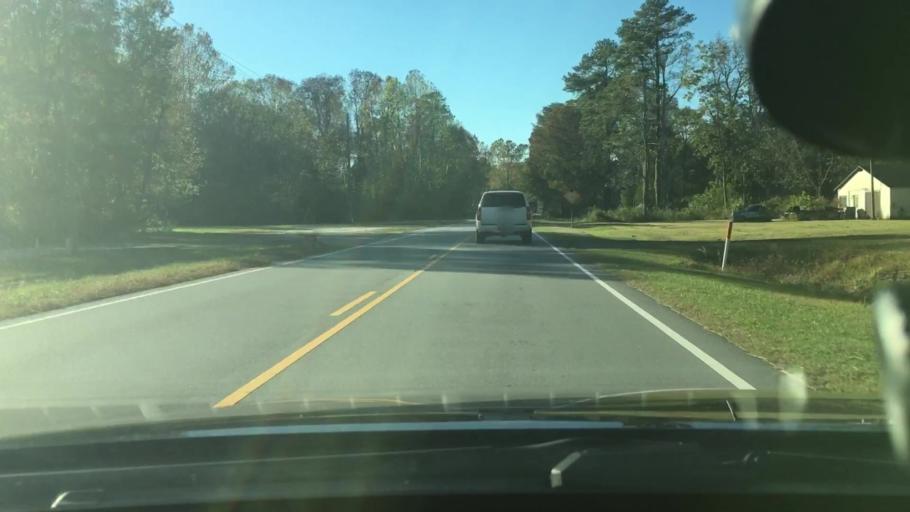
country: US
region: North Carolina
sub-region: Craven County
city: Vanceboro
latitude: 35.2944
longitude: -77.1433
